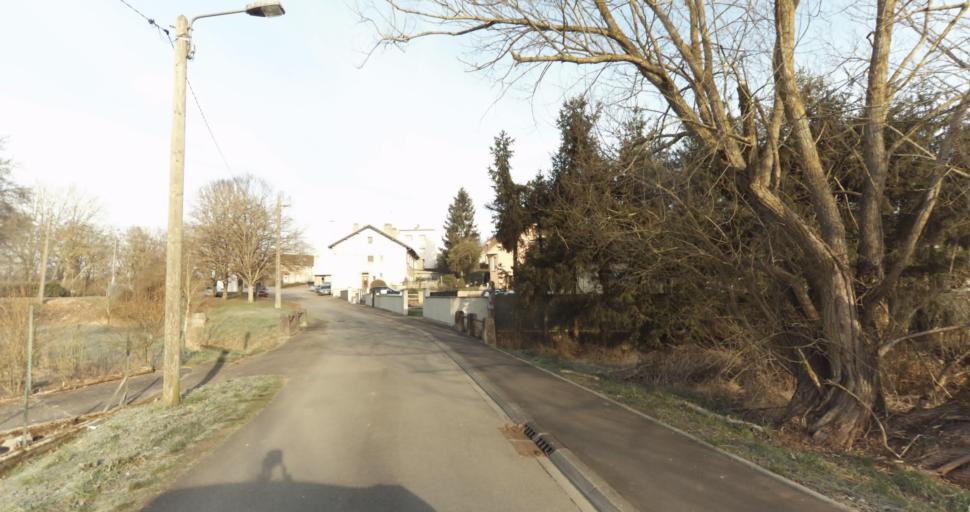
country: FR
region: Lorraine
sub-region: Departement de Meurthe-et-Moselle
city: Jarny
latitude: 49.1621
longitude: 5.8902
